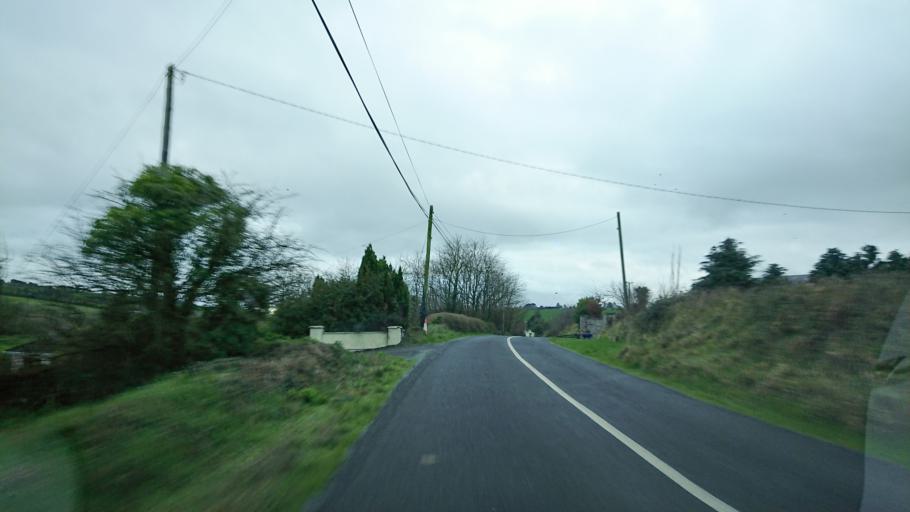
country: IE
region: Munster
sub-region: Waterford
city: Portlaw
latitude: 52.1590
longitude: -7.3844
